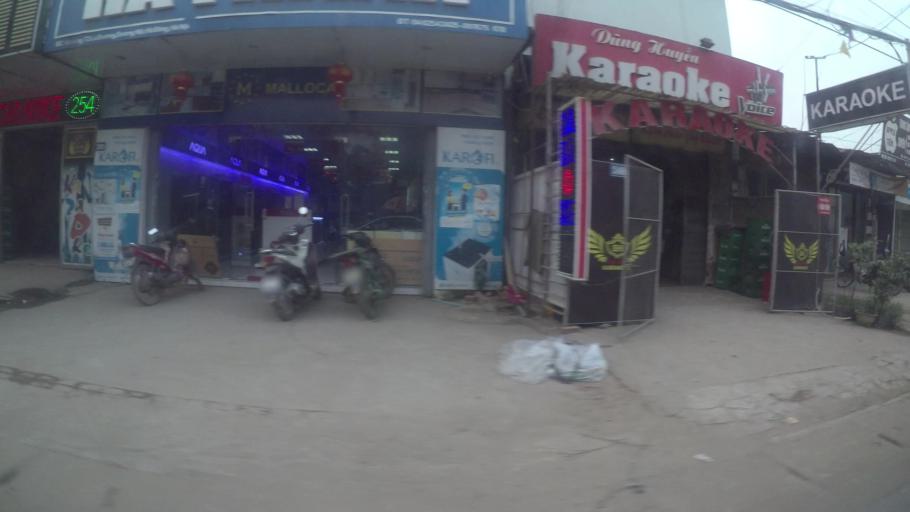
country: VN
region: Ha Noi
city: Ha Dong
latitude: 20.9925
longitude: 105.7324
